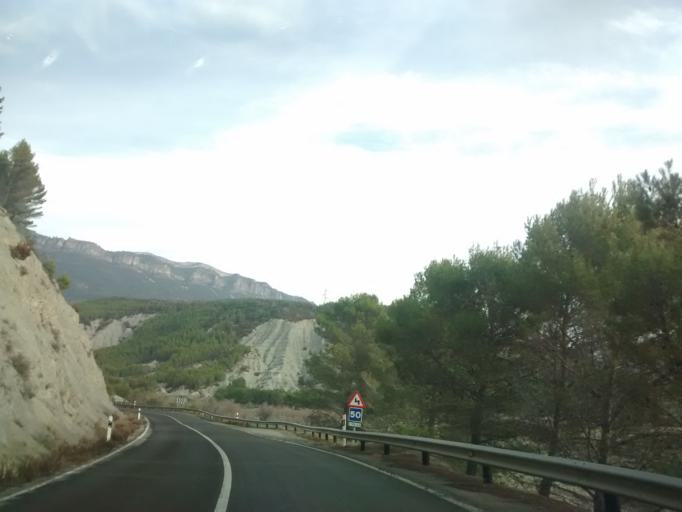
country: ES
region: Aragon
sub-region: Provincia de Zaragoza
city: Siguees
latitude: 42.6107
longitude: -1.0864
